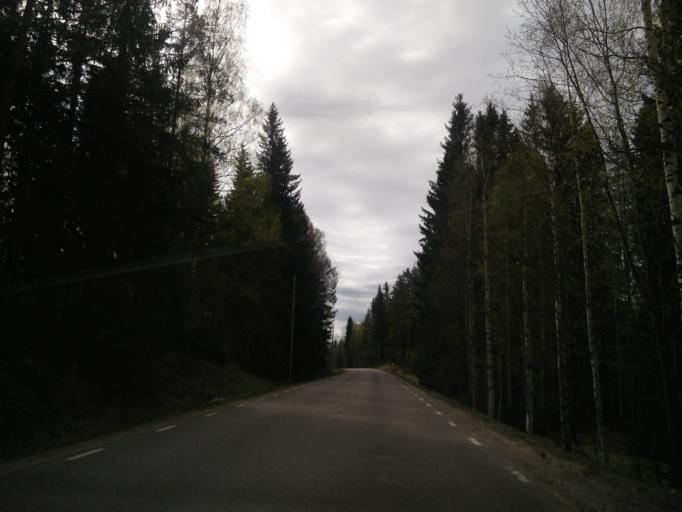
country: SE
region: Vaesternorrland
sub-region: Sundsvalls Kommun
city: Vi
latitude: 62.2631
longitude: 17.0855
